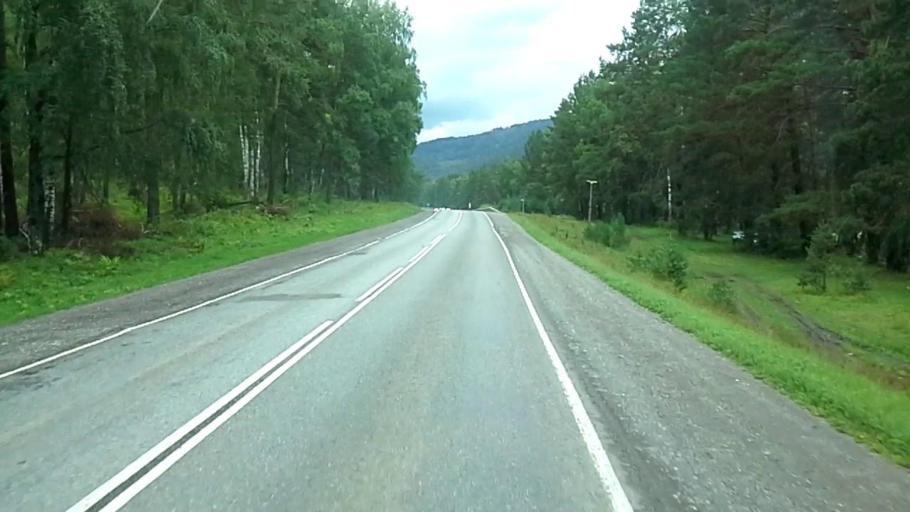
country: RU
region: Altay
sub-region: Mayminskiy Rayon
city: Manzherok
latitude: 51.8126
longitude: 85.7654
